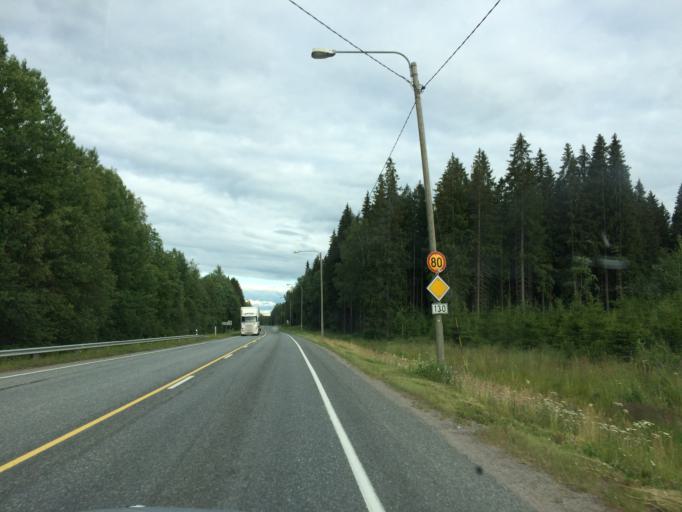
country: FI
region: Haeme
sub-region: Haemeenlinna
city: Haemeenlinna
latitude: 60.9553
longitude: 24.4932
